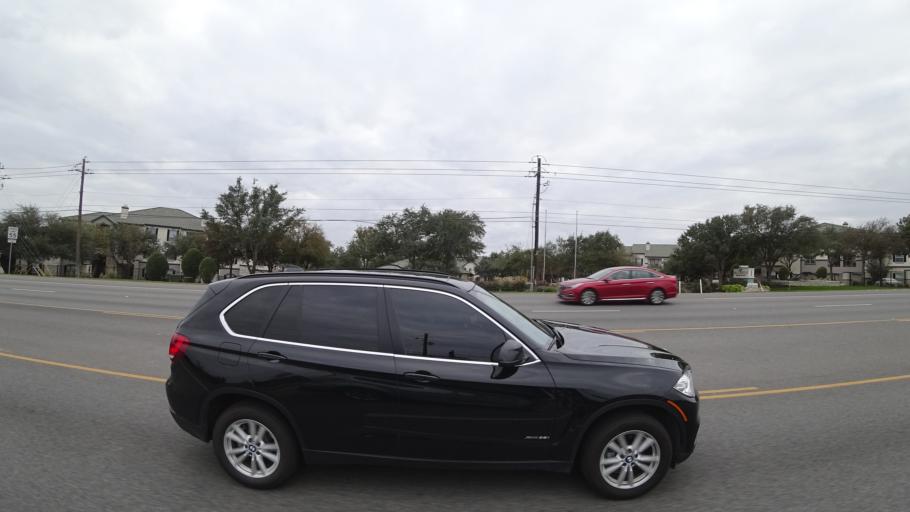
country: US
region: Texas
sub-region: Travis County
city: Bee Cave
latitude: 30.3262
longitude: -97.9626
